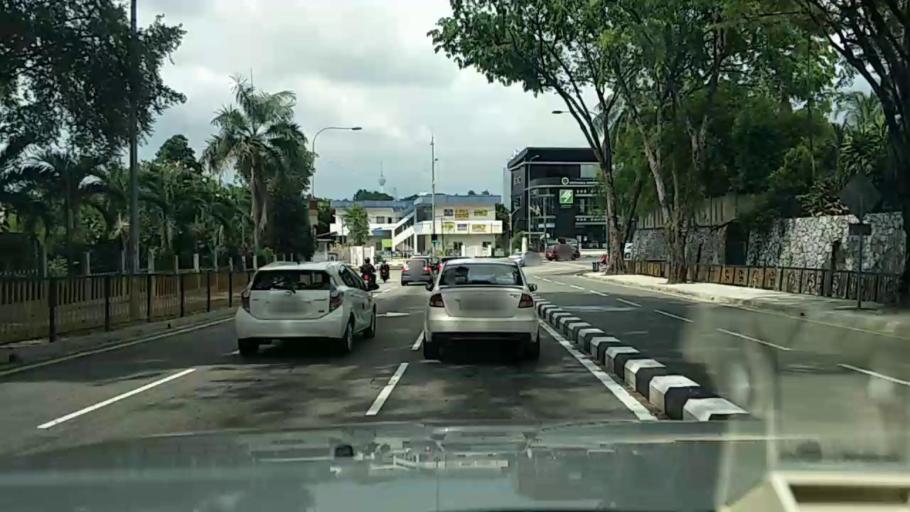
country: MY
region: Kuala Lumpur
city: Kuala Lumpur
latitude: 3.1294
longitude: 101.6724
